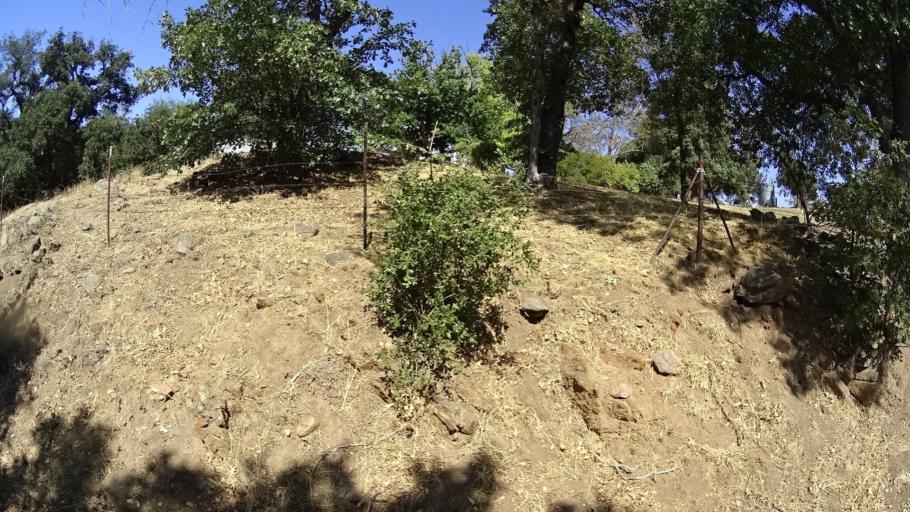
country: US
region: California
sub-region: San Diego County
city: Julian
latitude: 33.0665
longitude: -116.5869
